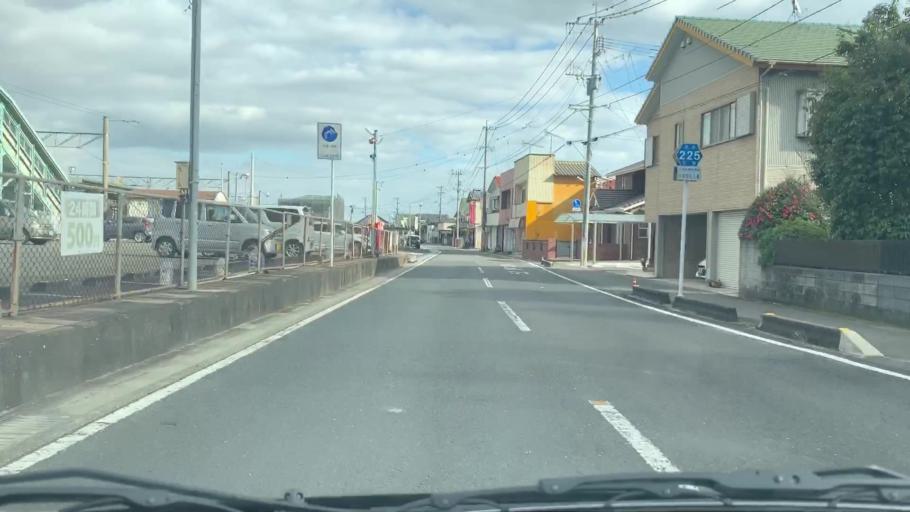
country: JP
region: Saga Prefecture
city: Saga-shi
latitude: 33.2553
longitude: 130.2288
